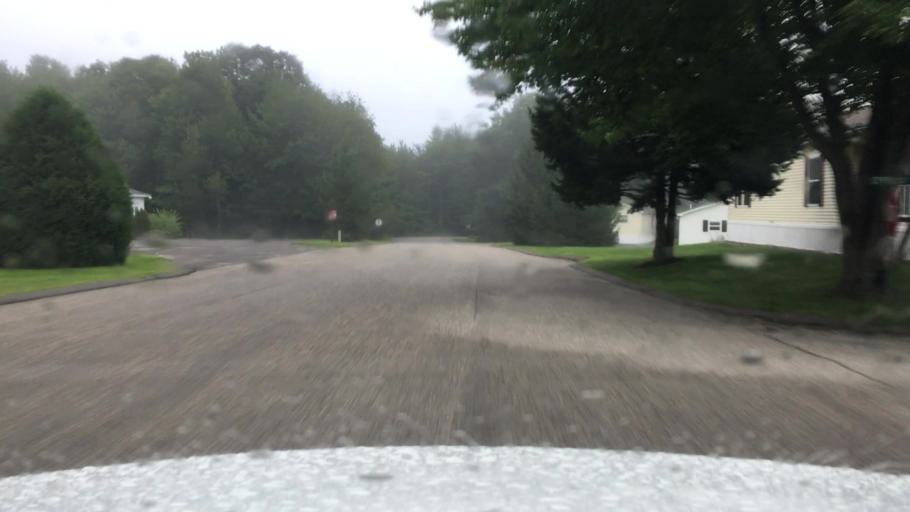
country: US
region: Maine
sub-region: Cumberland County
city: Scarborough
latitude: 43.5987
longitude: -70.3167
